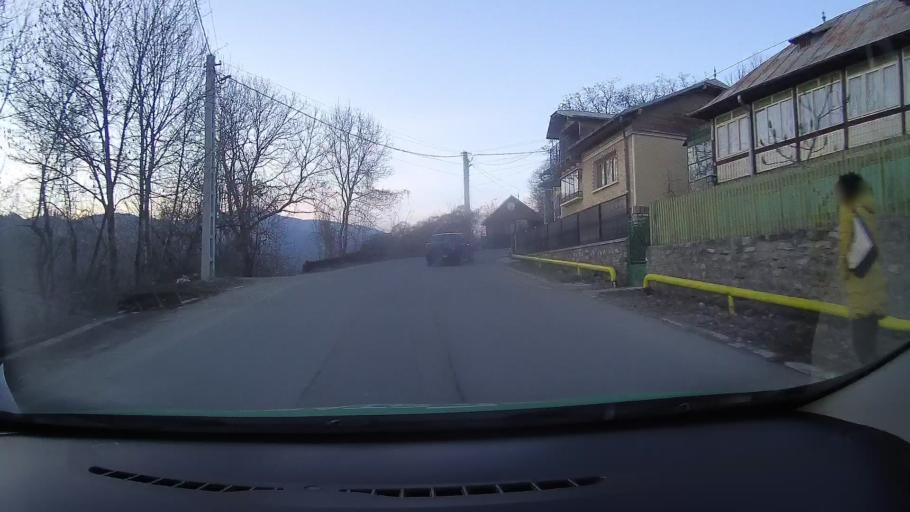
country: RO
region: Prahova
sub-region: Comuna Comarnic
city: Comarnic
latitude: 45.2449
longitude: 25.6326
